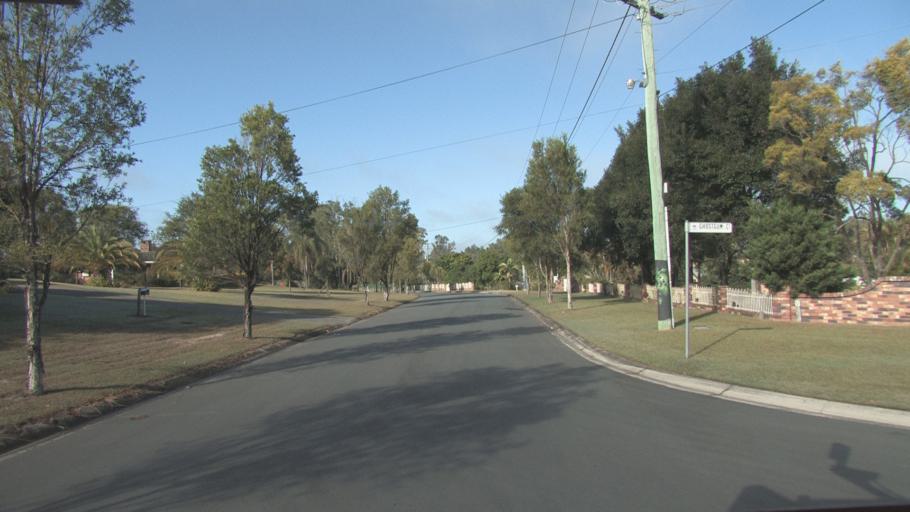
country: AU
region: Queensland
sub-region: Logan
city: Park Ridge South
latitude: -27.6967
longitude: 153.0324
